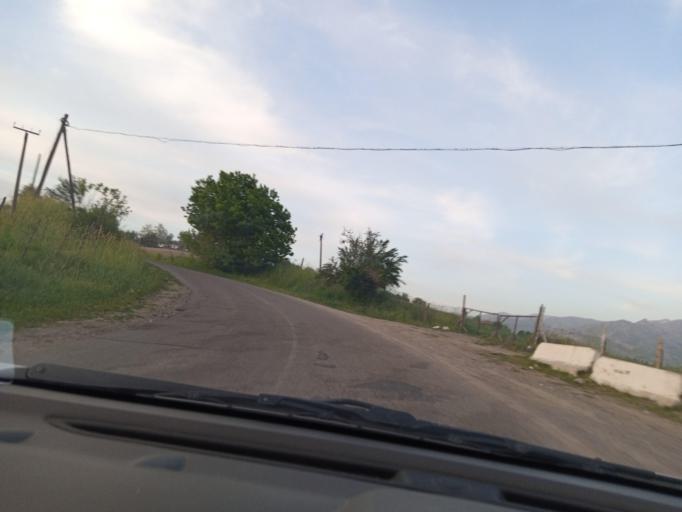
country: UZ
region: Toshkent
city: Parkent
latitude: 41.2435
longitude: 69.7318
